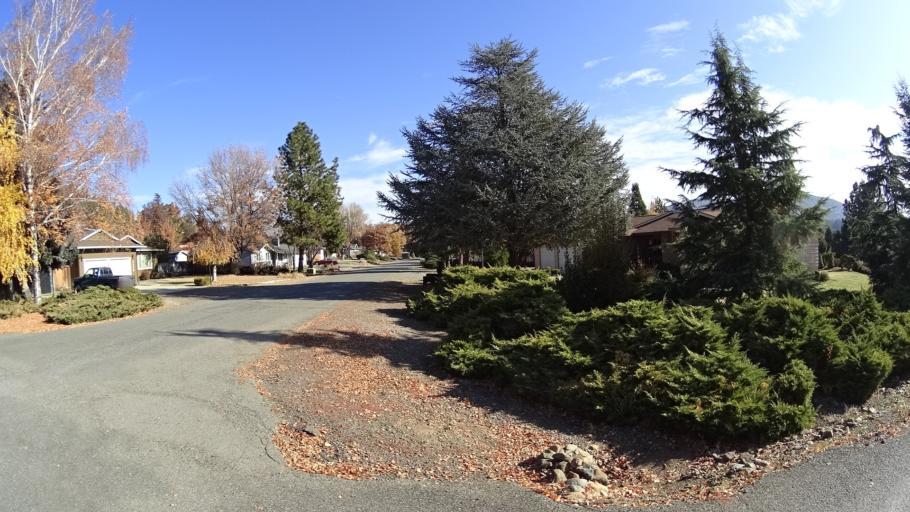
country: US
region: California
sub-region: Siskiyou County
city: Yreka
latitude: 41.6916
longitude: -122.6534
